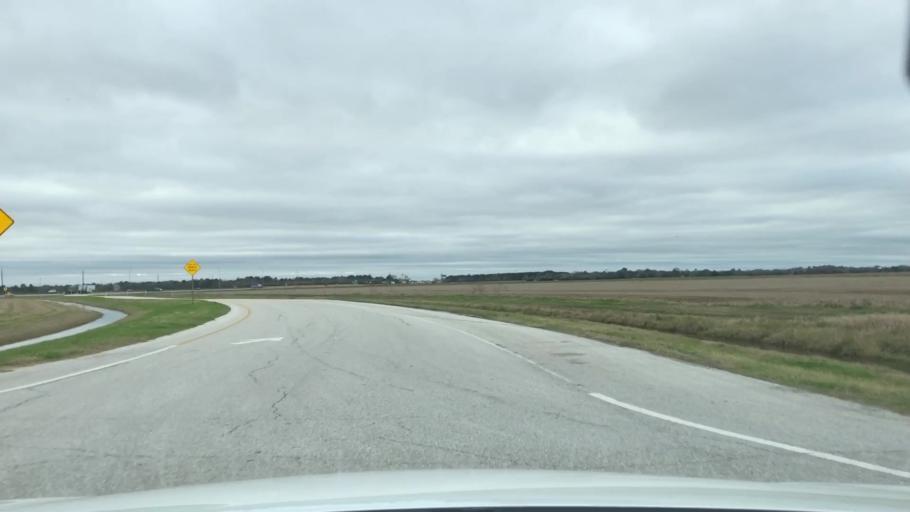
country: US
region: Texas
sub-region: Waller County
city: Brookshire
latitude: 29.7789
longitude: -95.9206
